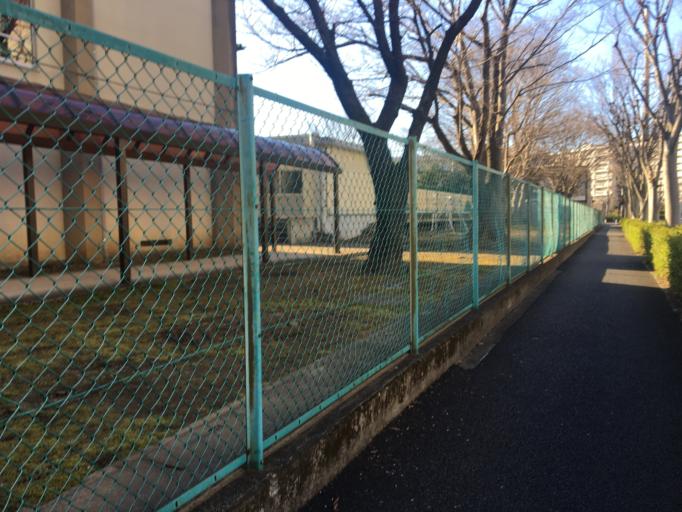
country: JP
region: Saitama
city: Shiki
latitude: 35.8277
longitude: 139.5635
